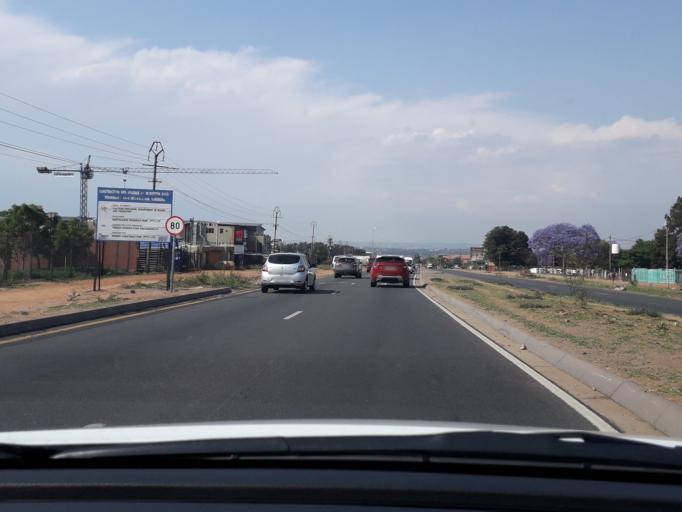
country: ZA
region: Gauteng
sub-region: West Rand District Municipality
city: Muldersdriseloop
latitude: -26.0426
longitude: 27.9562
